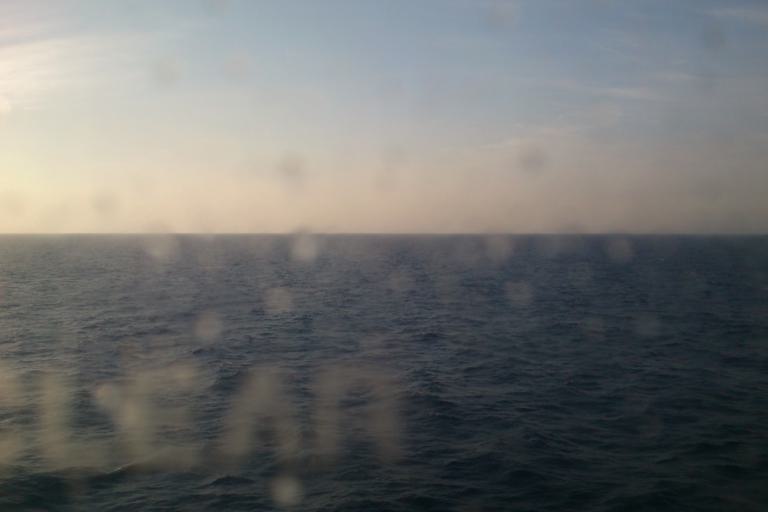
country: JP
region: Ishikawa
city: Nanao
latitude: 37.6871
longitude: 136.3683
